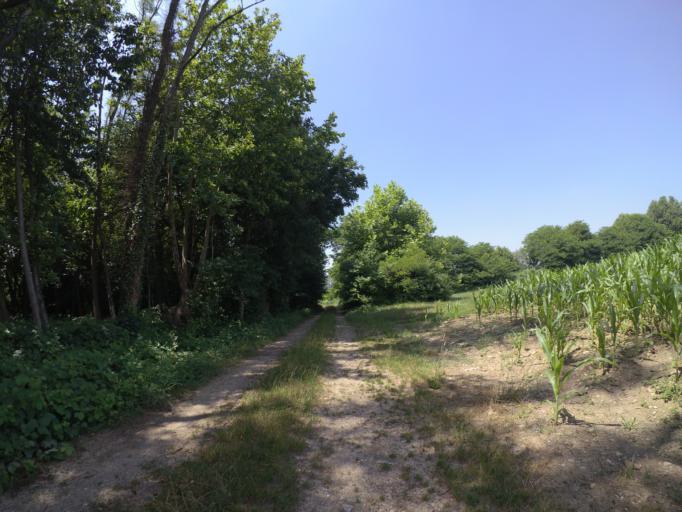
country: IT
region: Friuli Venezia Giulia
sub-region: Provincia di Udine
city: Bertiolo
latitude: 45.9299
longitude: 13.0467
